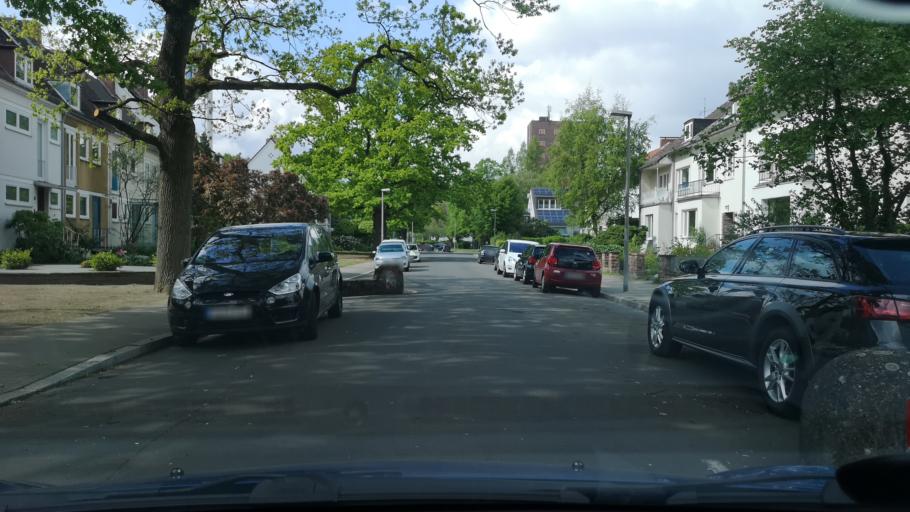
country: DE
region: Lower Saxony
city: Hannover
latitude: 52.3533
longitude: 9.7661
